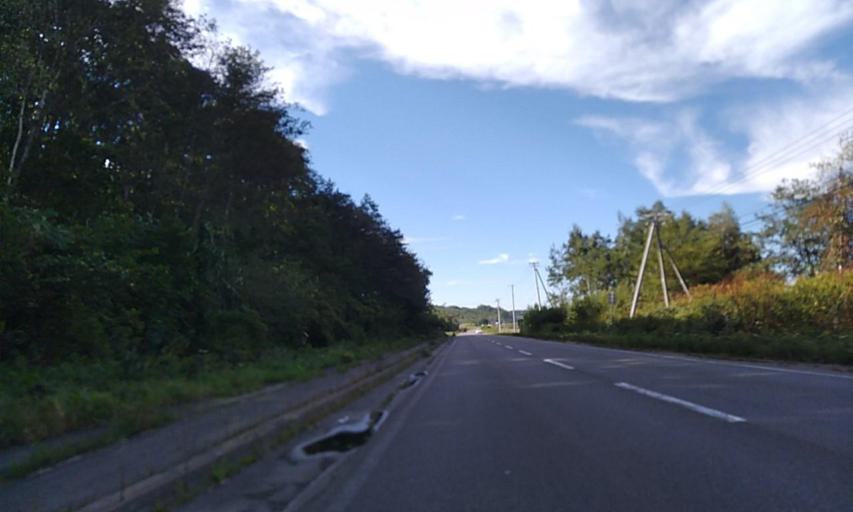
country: JP
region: Hokkaido
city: Obihiro
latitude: 42.8181
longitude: 143.4851
